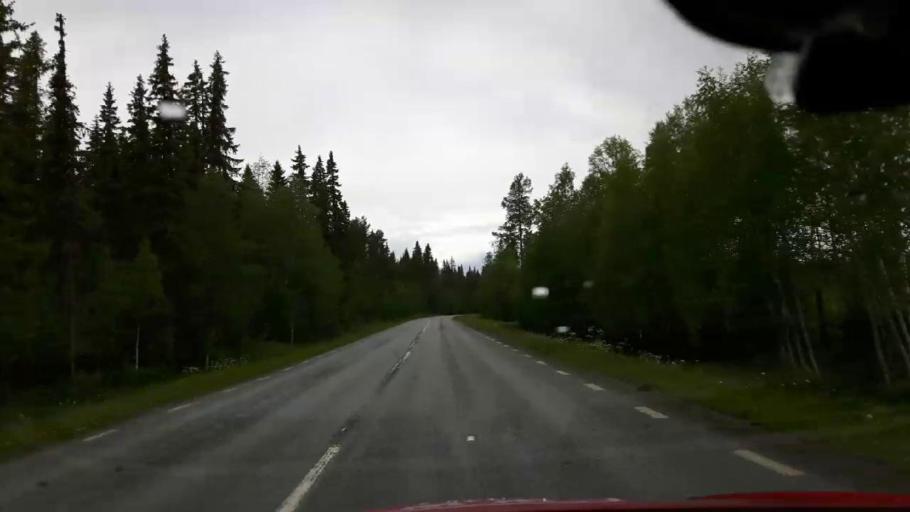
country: SE
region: Jaemtland
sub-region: Krokoms Kommun
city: Krokom
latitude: 63.4276
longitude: 14.2123
